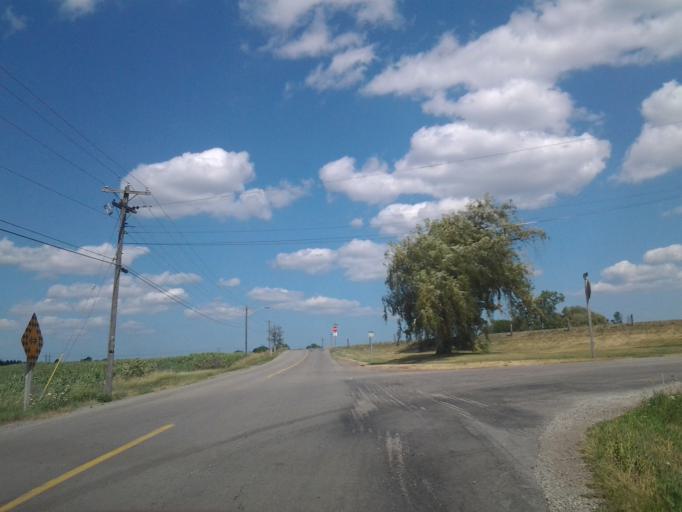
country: CA
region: Ontario
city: Ancaster
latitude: 43.2873
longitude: -79.9512
